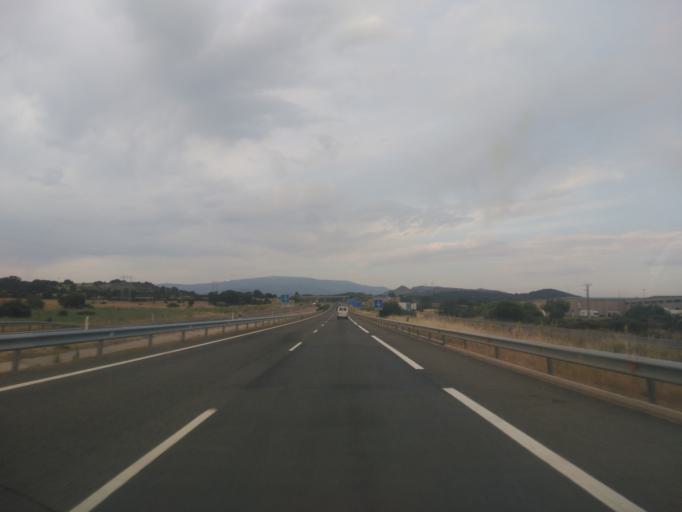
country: ES
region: Castille and Leon
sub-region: Provincia de Salamanca
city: Fuentes de Bejar
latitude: 40.5099
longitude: -5.6747
